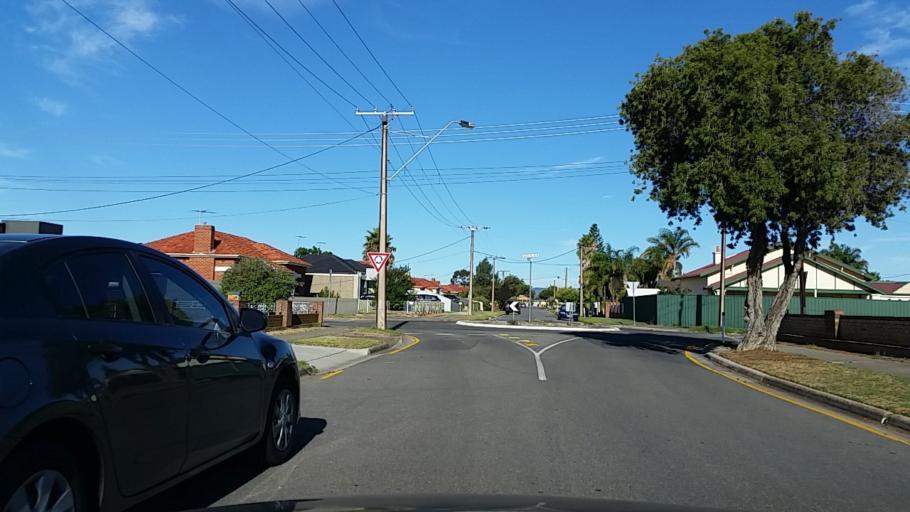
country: AU
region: South Australia
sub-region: Charles Sturt
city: Seaton
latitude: -34.8898
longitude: 138.5192
